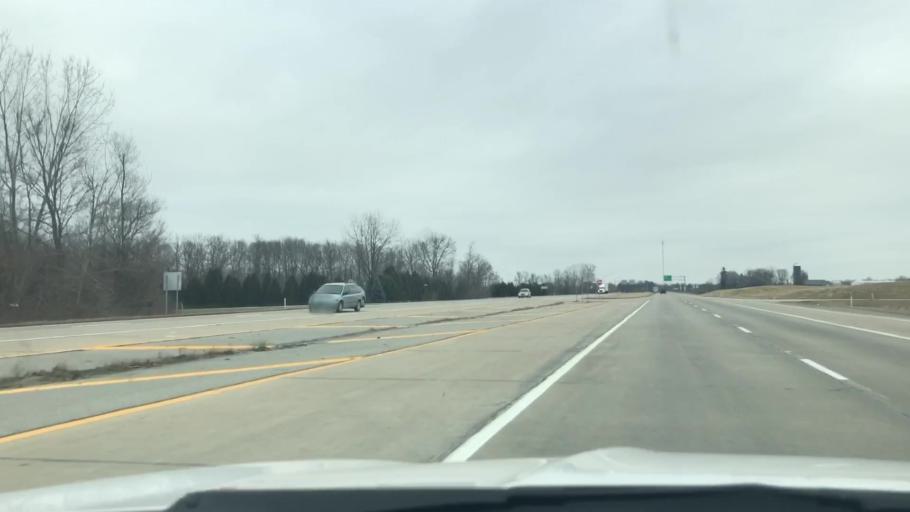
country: US
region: Indiana
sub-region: Cass County
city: Logansport
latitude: 40.7314
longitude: -86.3139
